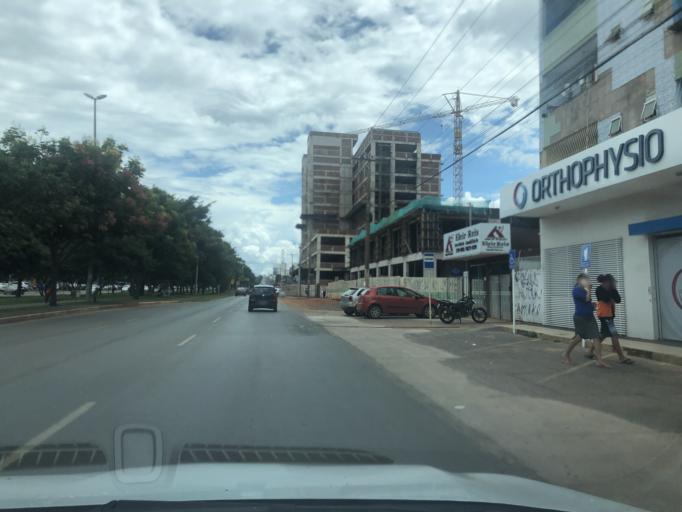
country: BR
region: Federal District
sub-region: Brasilia
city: Brasilia
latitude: -15.8715
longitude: -48.0663
